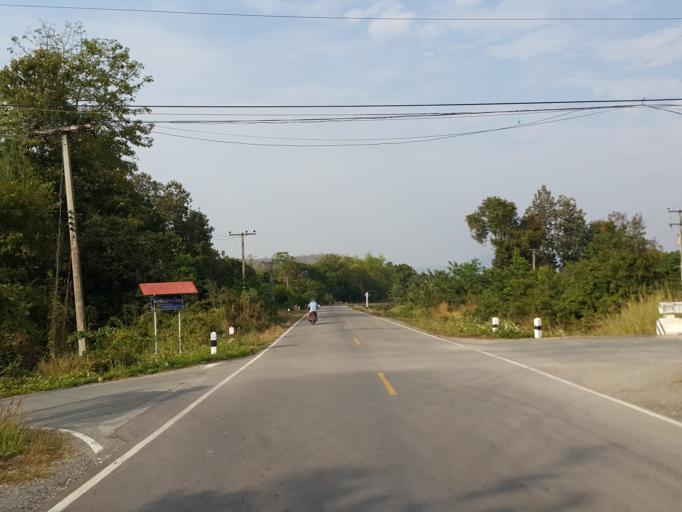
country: TH
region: Chiang Mai
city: San Sai
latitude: 18.8530
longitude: 99.1466
